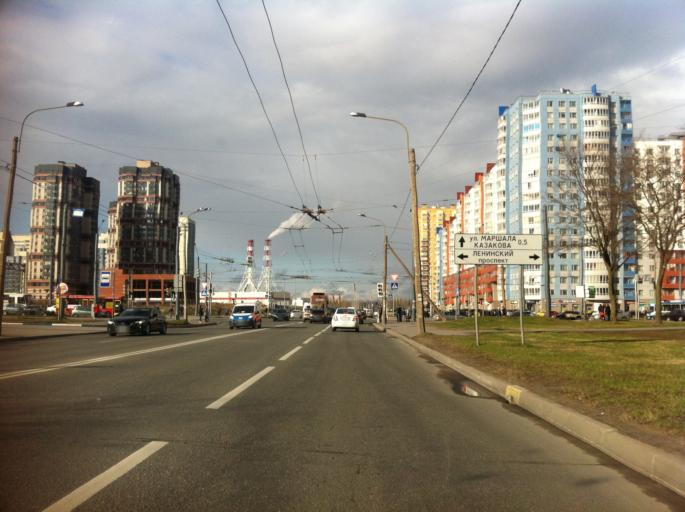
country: RU
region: St.-Petersburg
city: Uritsk
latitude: 59.8606
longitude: 30.1791
